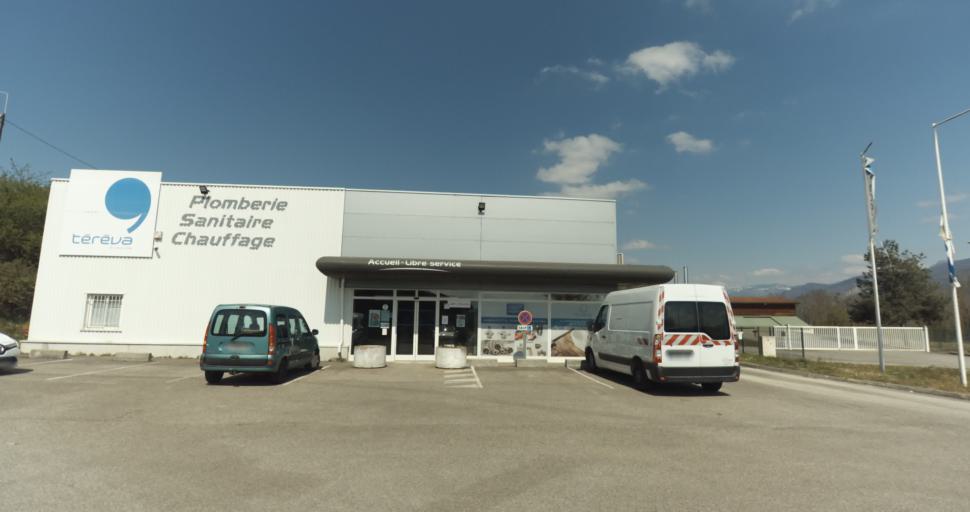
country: FR
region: Rhone-Alpes
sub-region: Departement de l'Isere
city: Saint-Marcellin
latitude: 45.1427
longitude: 5.3270
